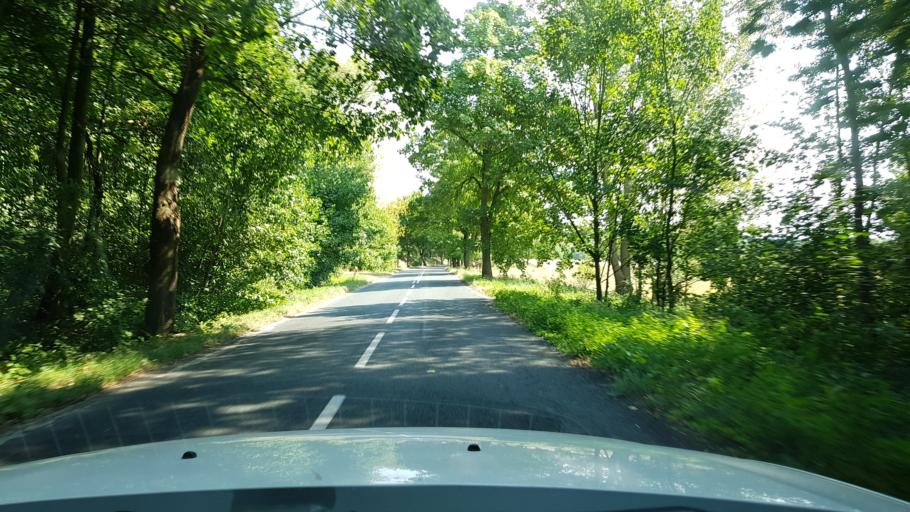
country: PL
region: West Pomeranian Voivodeship
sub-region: Powiat gryfinski
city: Cedynia
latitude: 52.8324
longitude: 14.2083
